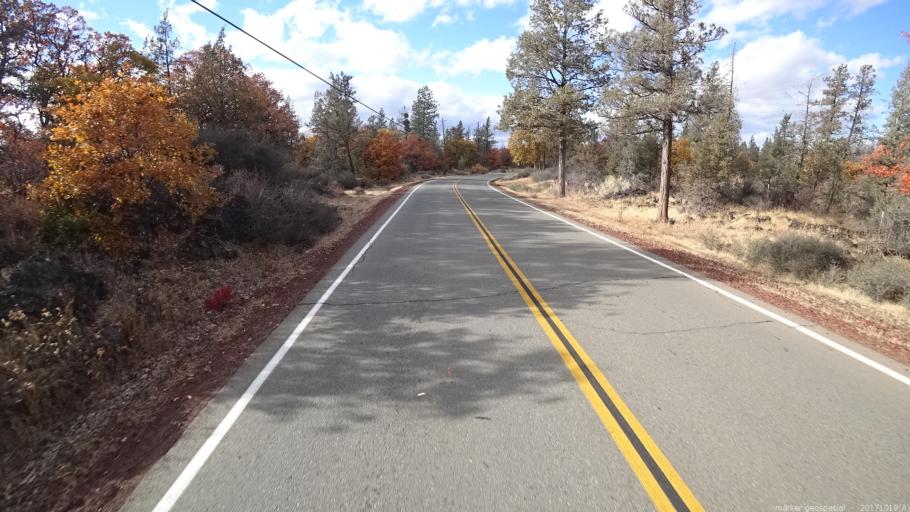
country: US
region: California
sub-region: Shasta County
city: Burney
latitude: 40.9958
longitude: -121.4328
